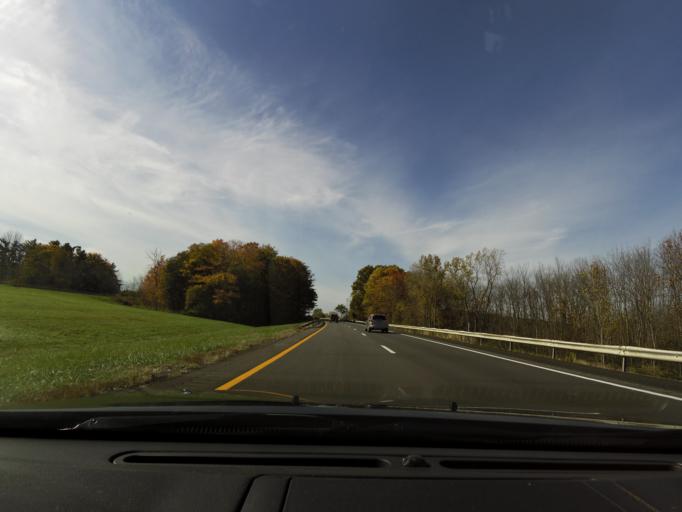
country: US
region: New York
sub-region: Erie County
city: Billington Heights
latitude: 42.7971
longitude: -78.6090
